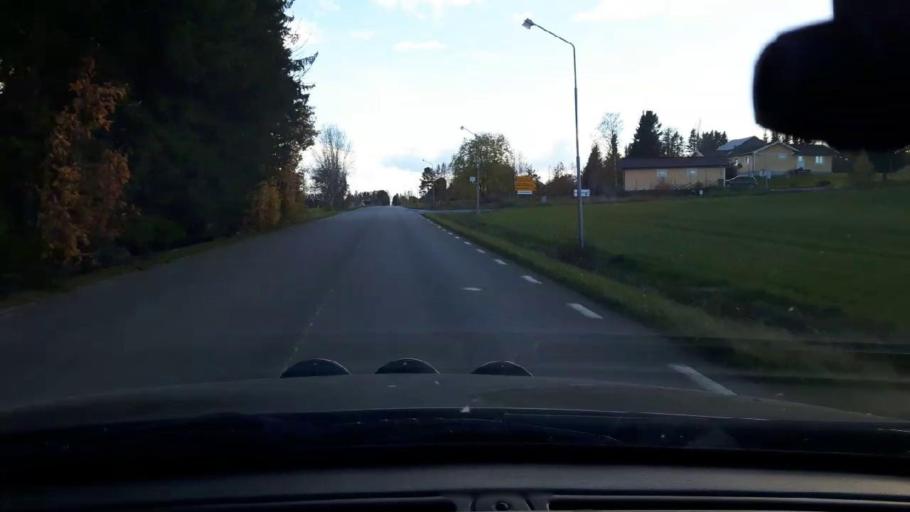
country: SE
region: Jaemtland
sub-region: Bergs Kommun
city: Hoverberg
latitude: 63.0203
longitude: 14.3432
